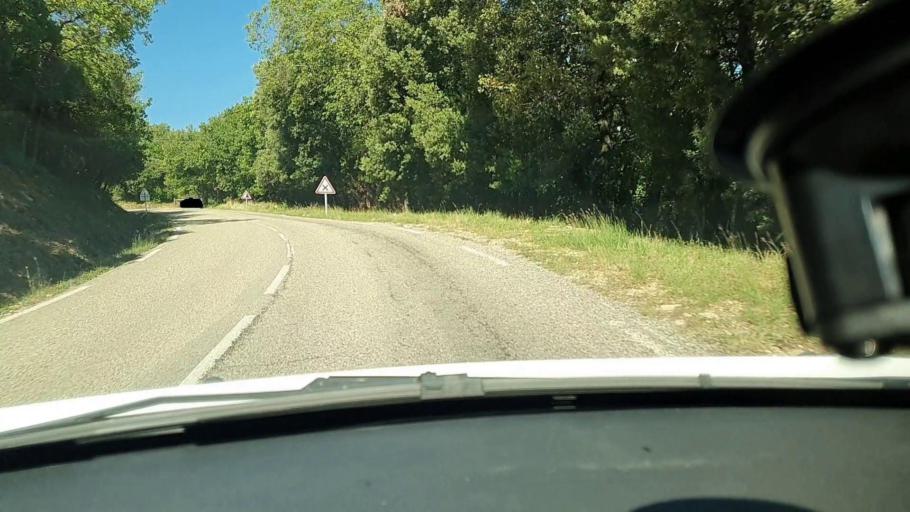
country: FR
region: Languedoc-Roussillon
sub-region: Departement du Gard
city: Saint-Paulet-de-Caisson
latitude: 44.2402
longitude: 4.5652
